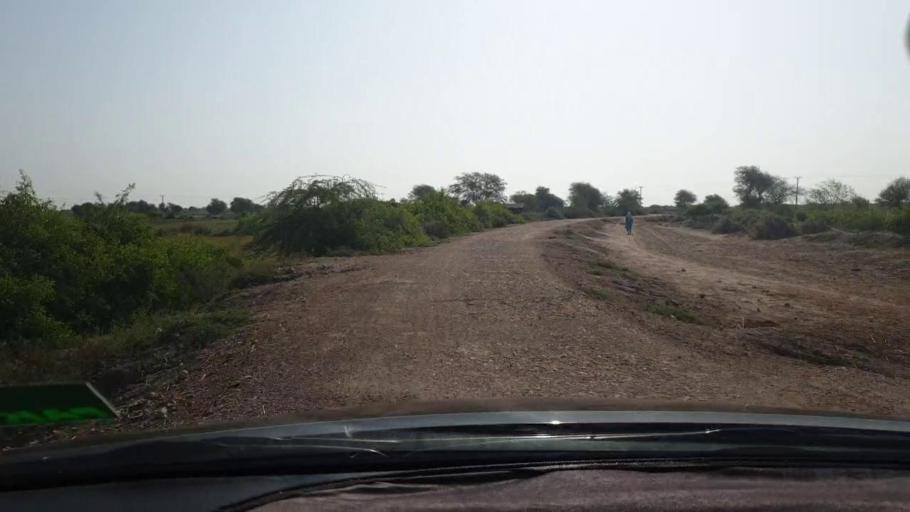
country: PK
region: Sindh
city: Tando Bago
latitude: 24.7124
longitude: 68.9858
